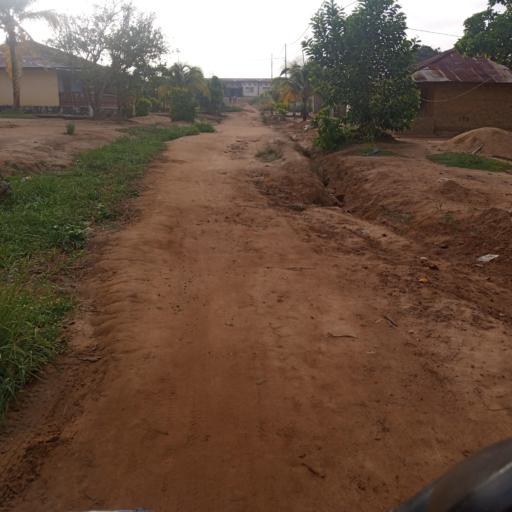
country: SL
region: Eastern Province
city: Pendembu
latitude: 8.0978
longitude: -10.6915
